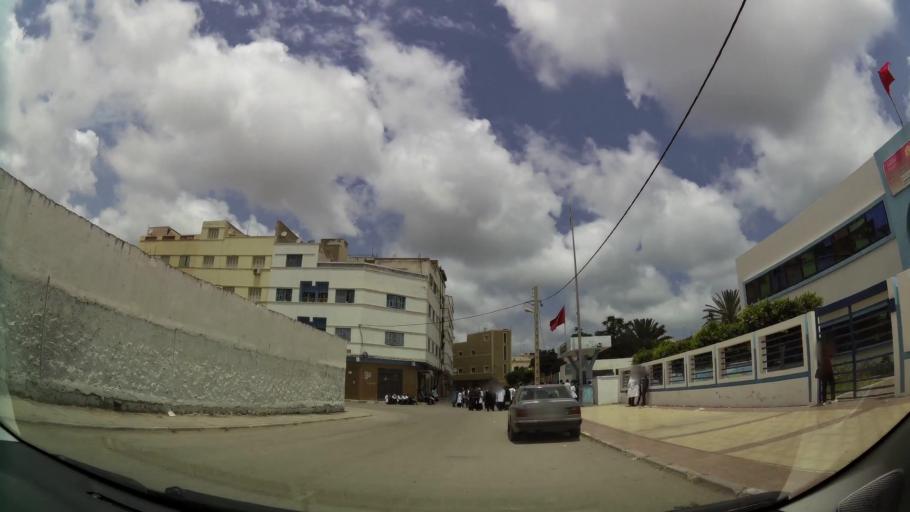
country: MA
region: Oriental
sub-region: Nador
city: Nador
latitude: 35.1719
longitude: -2.9221
